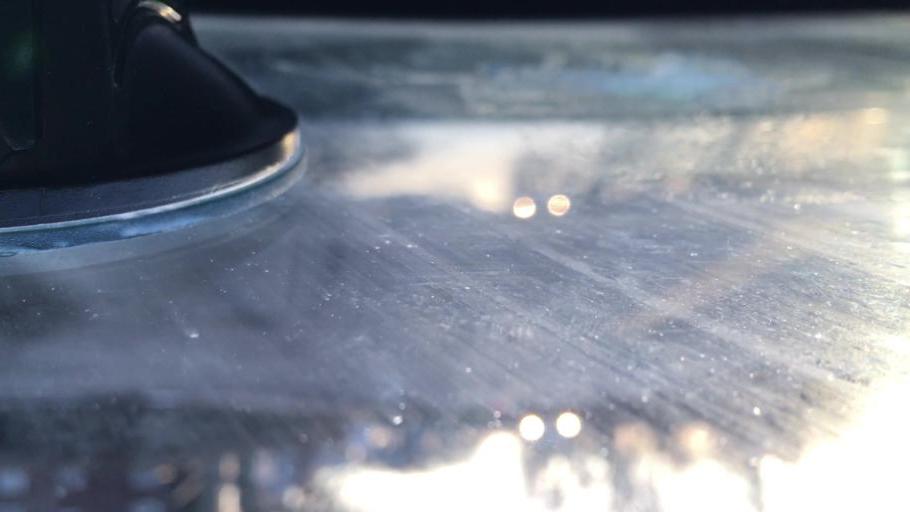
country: US
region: Massachusetts
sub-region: Middlesex County
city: Watertown
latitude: 42.3819
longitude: -71.1959
